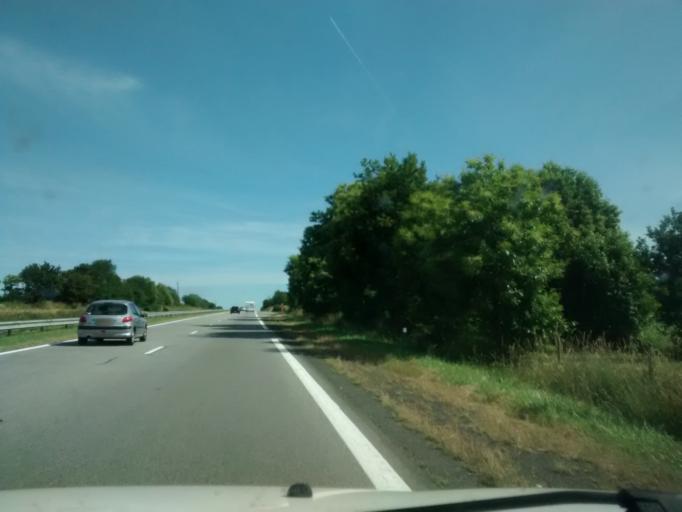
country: FR
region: Brittany
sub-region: Departement d'Ille-et-Vilaine
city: Quedillac
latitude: 48.2444
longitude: -2.1311
